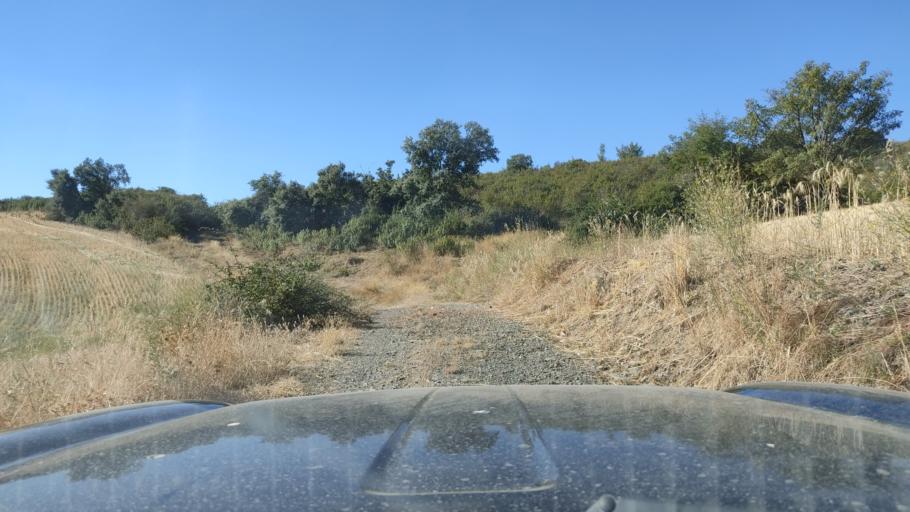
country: ES
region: Aragon
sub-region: Provincia de Teruel
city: Monforte de Moyuela
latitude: 41.0240
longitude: -1.0081
